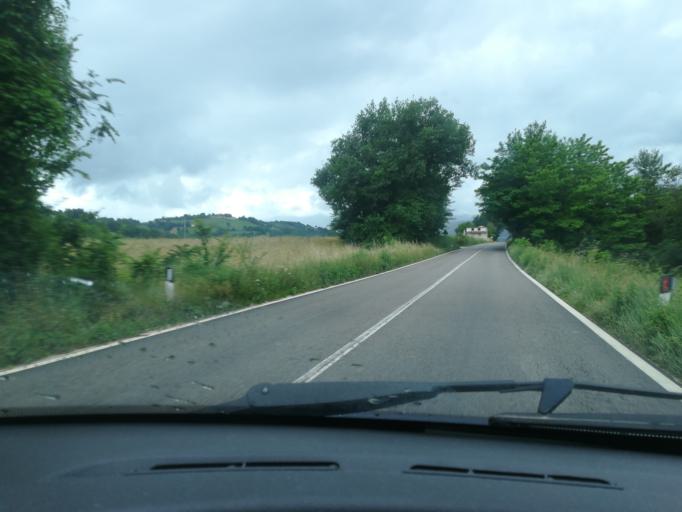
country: IT
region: The Marches
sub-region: Provincia di Macerata
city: San Ginesio
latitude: 43.0937
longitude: 13.3215
